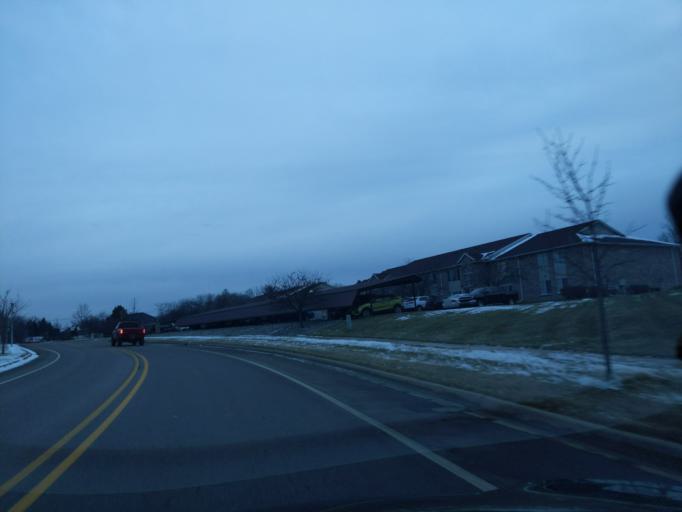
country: US
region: Michigan
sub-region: Ingham County
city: Mason
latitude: 42.5722
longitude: -84.4500
